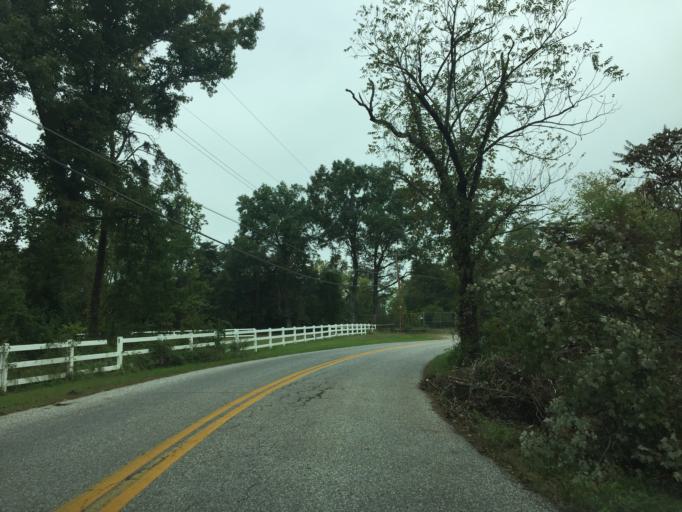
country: US
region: Maryland
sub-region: Baltimore County
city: Bowleys Quarters
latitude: 39.3688
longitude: -76.3904
